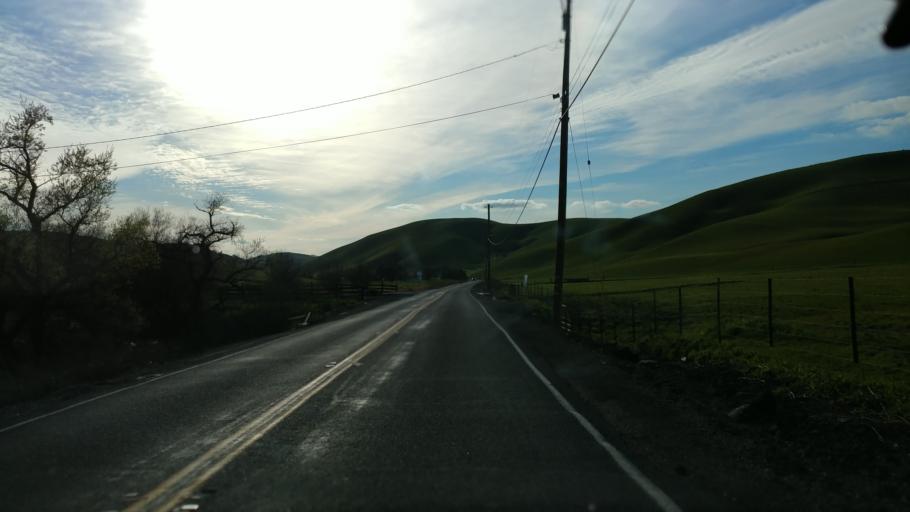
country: US
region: California
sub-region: Contra Costa County
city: Blackhawk
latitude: 37.7799
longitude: -121.8362
